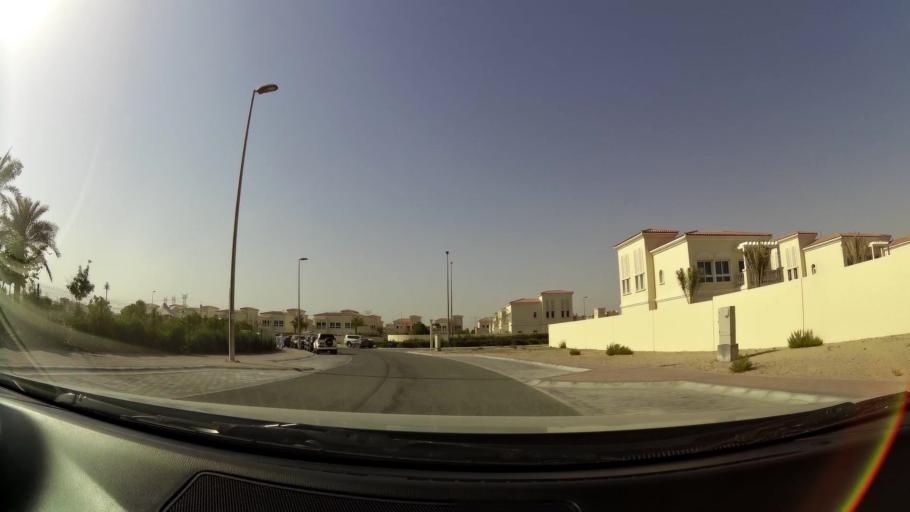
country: AE
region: Dubai
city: Dubai
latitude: 25.0705
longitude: 55.2119
